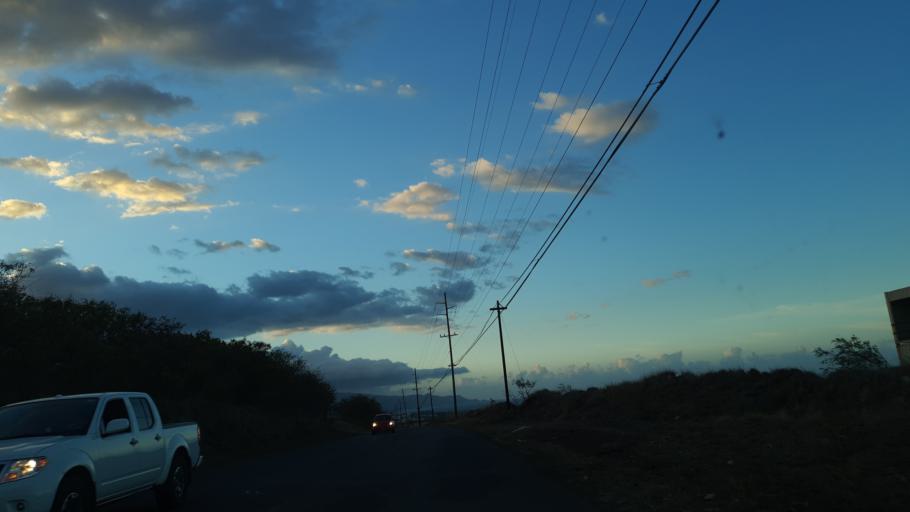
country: US
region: Hawaii
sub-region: Maui County
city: Kahului
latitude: 20.8593
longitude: -156.4254
